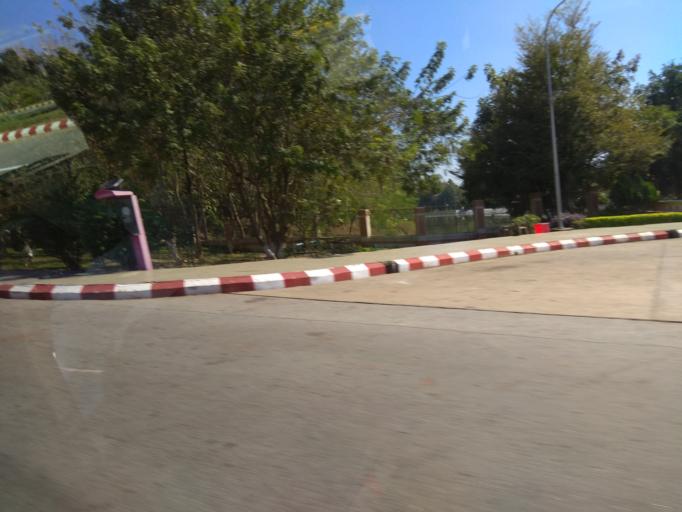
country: MM
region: Mandalay
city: Nay Pyi Taw
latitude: 19.7515
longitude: 96.1222
